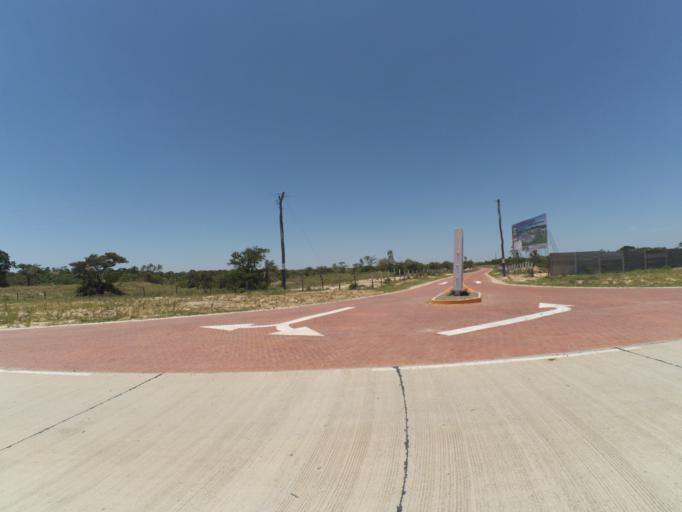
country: BO
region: Santa Cruz
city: Santa Cruz de la Sierra
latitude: -17.7848
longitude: -63.2711
